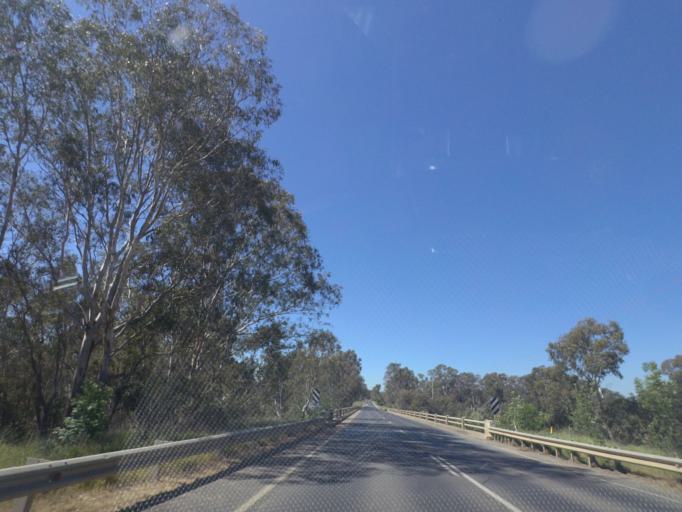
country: AU
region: Victoria
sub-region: Murrindindi
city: Kinglake West
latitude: -37.0281
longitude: 145.1074
